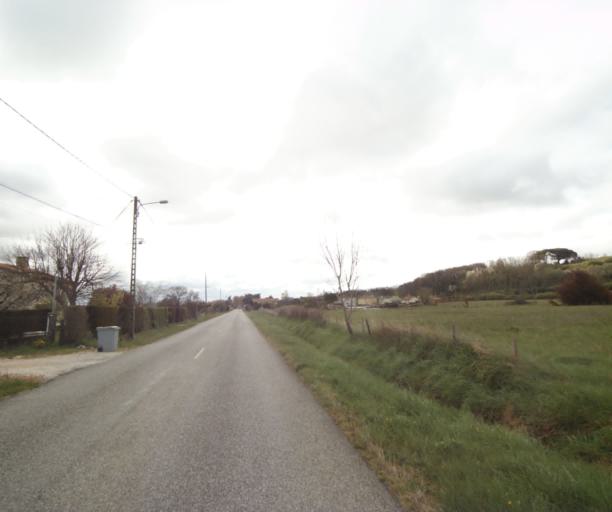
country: FR
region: Midi-Pyrenees
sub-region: Departement de l'Ariege
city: Saverdun
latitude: 43.2440
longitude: 1.5634
